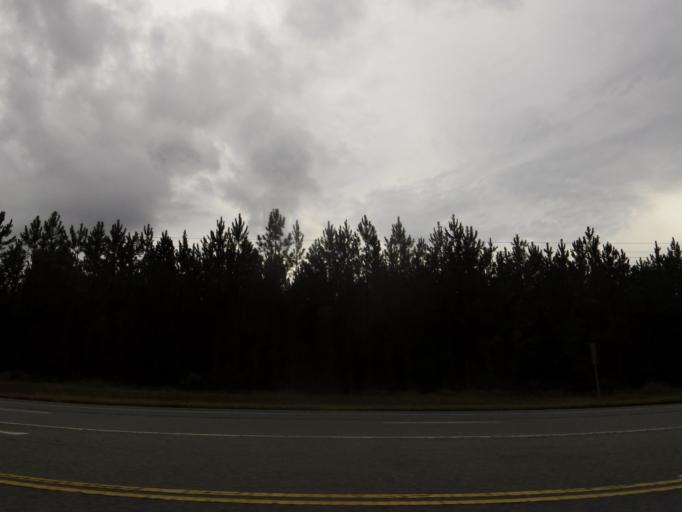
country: US
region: Georgia
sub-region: Wayne County
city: Jesup
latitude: 31.5561
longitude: -81.8226
